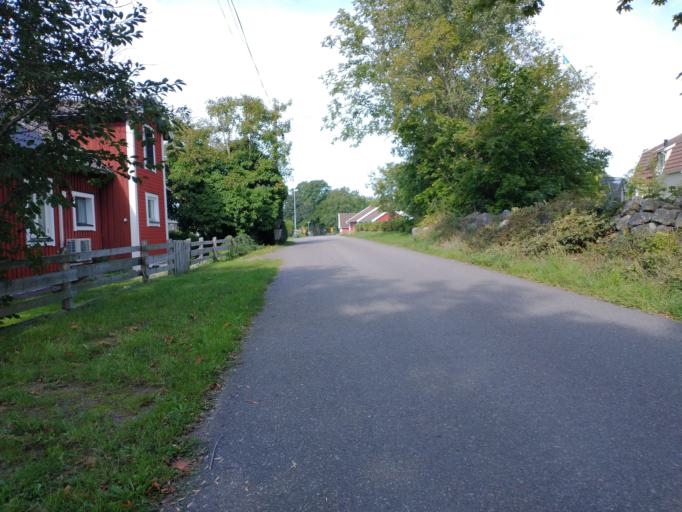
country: SE
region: Kalmar
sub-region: Kalmar Kommun
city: Lindsdal
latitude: 56.7785
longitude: 16.3066
